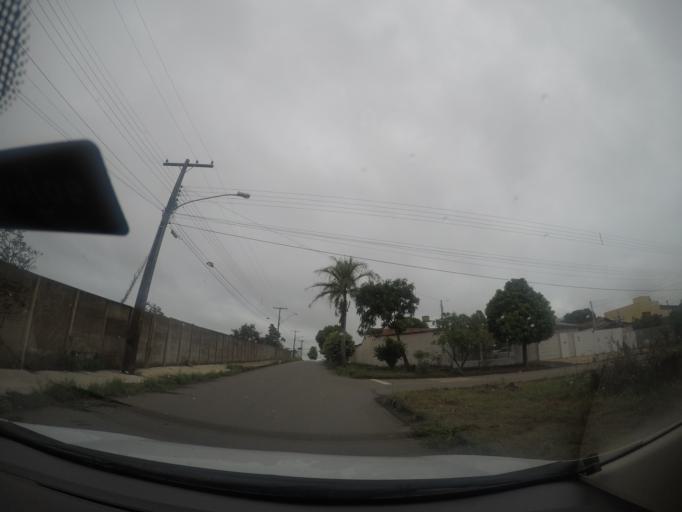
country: BR
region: Goias
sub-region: Goiania
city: Goiania
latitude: -16.7487
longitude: -49.3216
